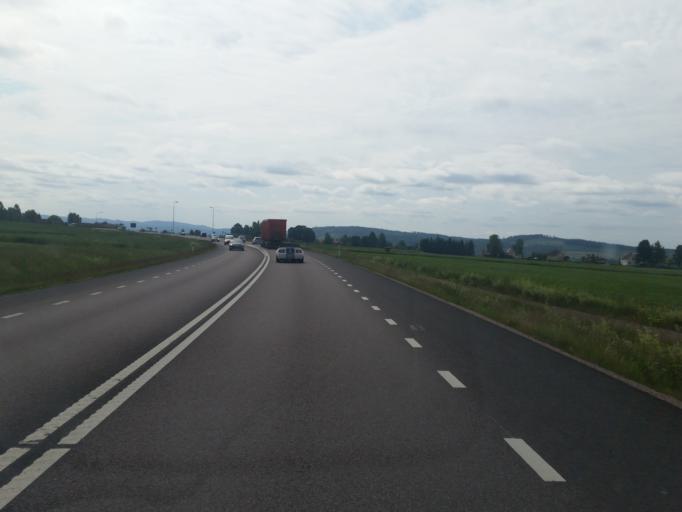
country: SE
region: Dalarna
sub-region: Gagnefs Kommun
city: Gagnef
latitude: 60.6072
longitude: 15.0510
